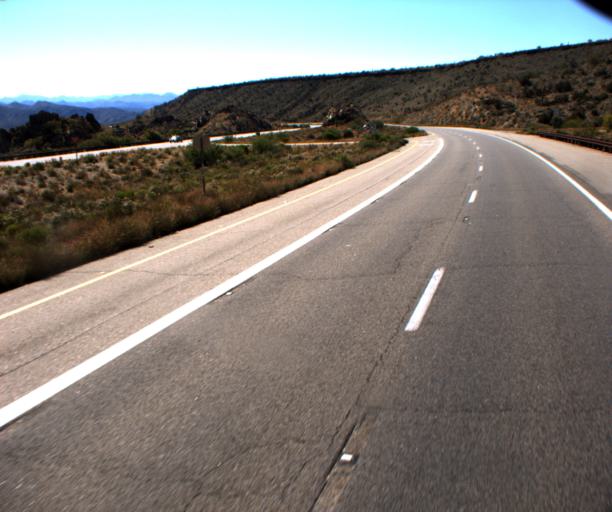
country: US
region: Arizona
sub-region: Yavapai County
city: Bagdad
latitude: 34.4521
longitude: -113.2880
